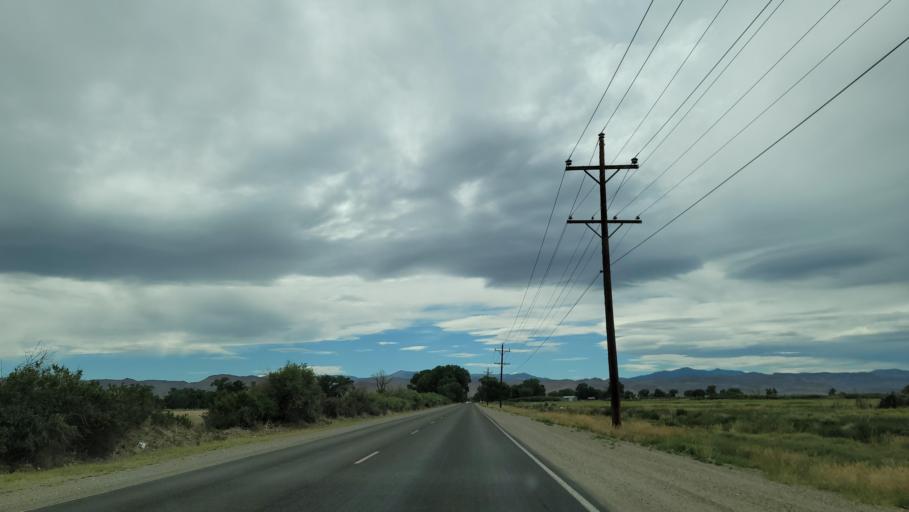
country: US
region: Nevada
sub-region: Lyon County
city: Yerington
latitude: 39.0482
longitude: -119.1477
